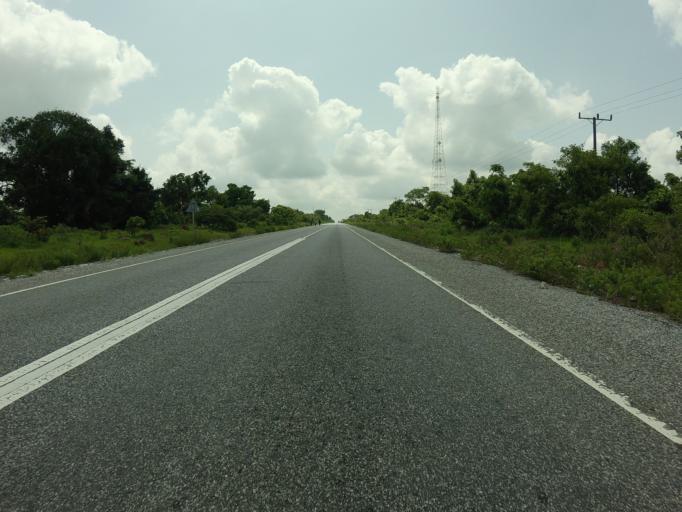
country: GH
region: Northern
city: Tamale
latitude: 9.1339
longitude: -1.5815
